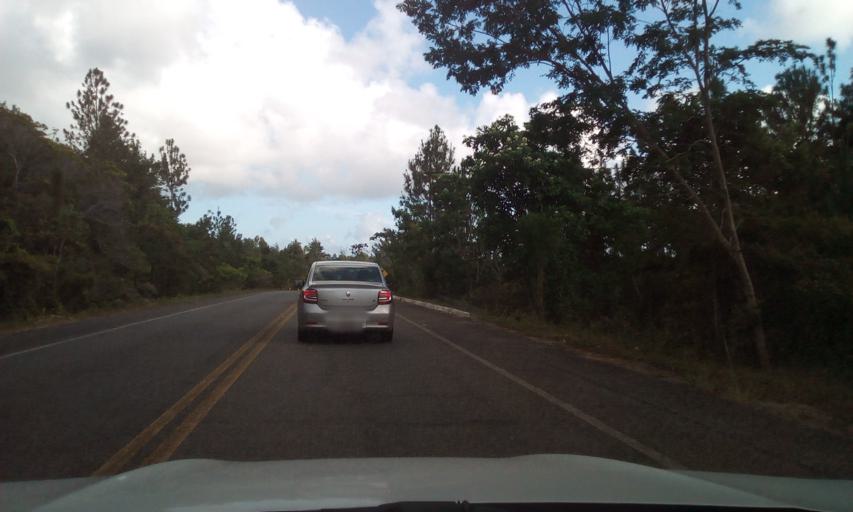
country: BR
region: Bahia
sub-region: Entre Rios
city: Entre Rios
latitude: -12.1327
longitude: -37.7918
